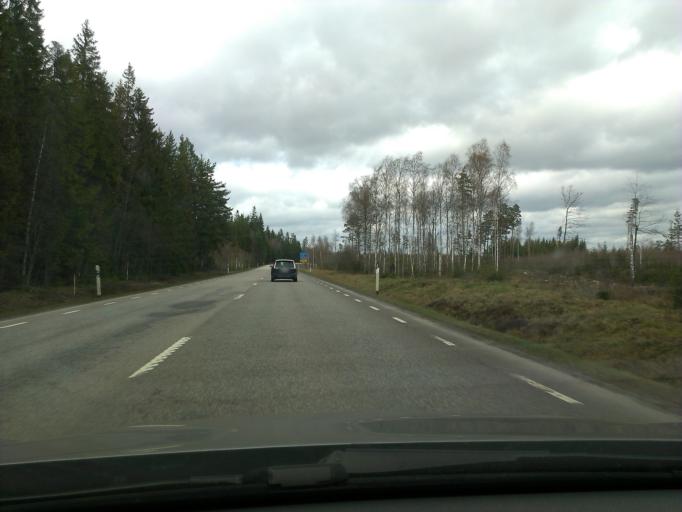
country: SE
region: Kronoberg
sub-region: Almhults Kommun
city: AElmhult
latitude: 56.5828
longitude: 14.1904
